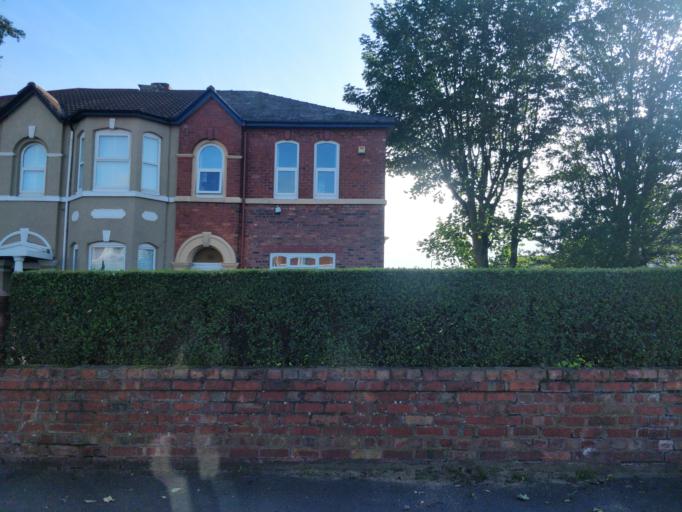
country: GB
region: England
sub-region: Sefton
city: Southport
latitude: 53.6471
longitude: -2.9874
